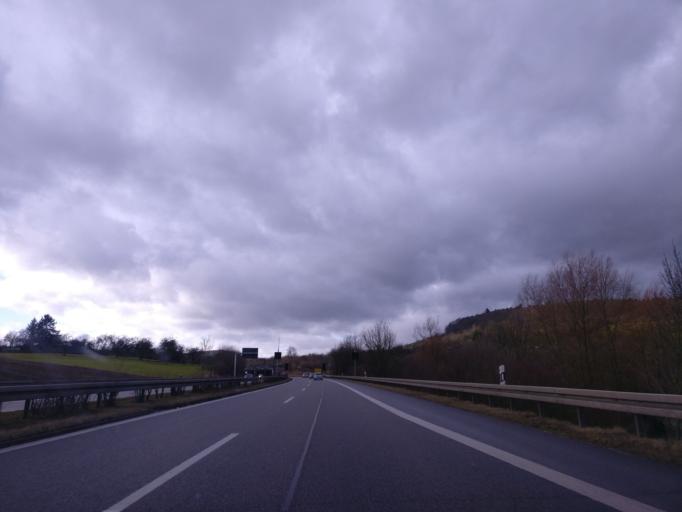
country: DE
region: Baden-Wuerttemberg
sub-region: Regierungsbezirk Stuttgart
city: Schorndorf
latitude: 48.8213
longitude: 9.5388
